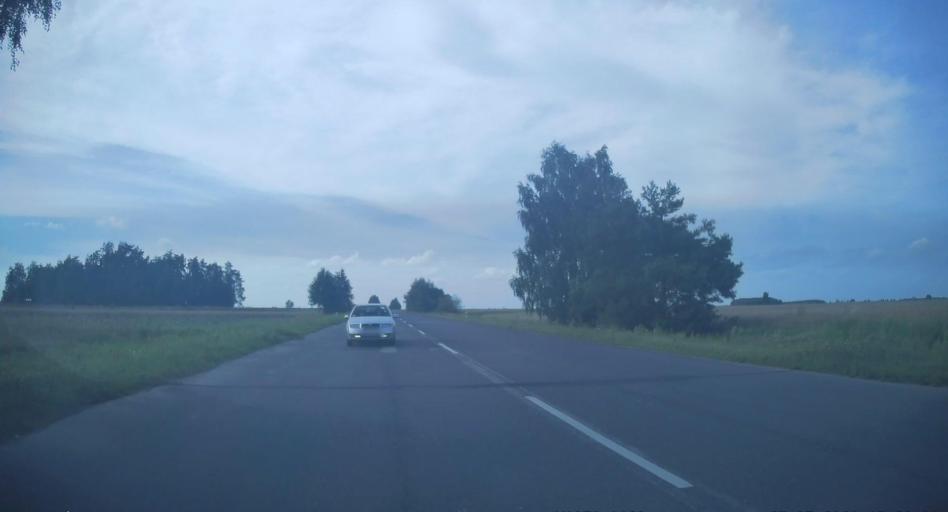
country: PL
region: Lodz Voivodeship
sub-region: Powiat tomaszowski
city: Rzeczyca
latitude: 51.6488
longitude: 20.2811
